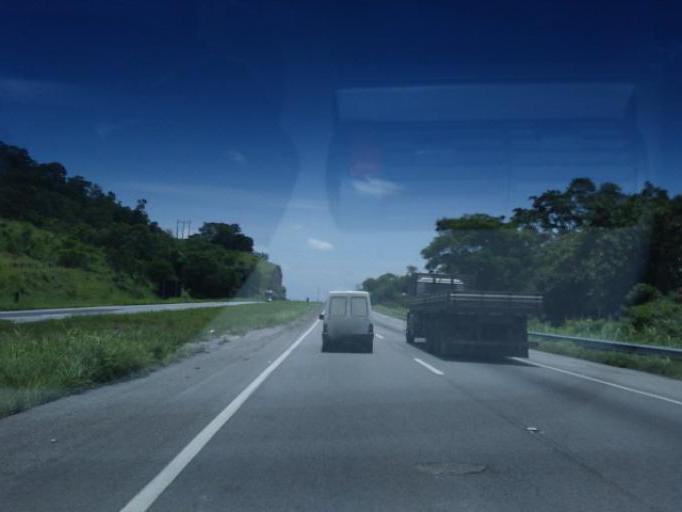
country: BR
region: Sao Paulo
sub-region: Juquia
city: Juquia
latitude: -24.3228
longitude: -47.5452
